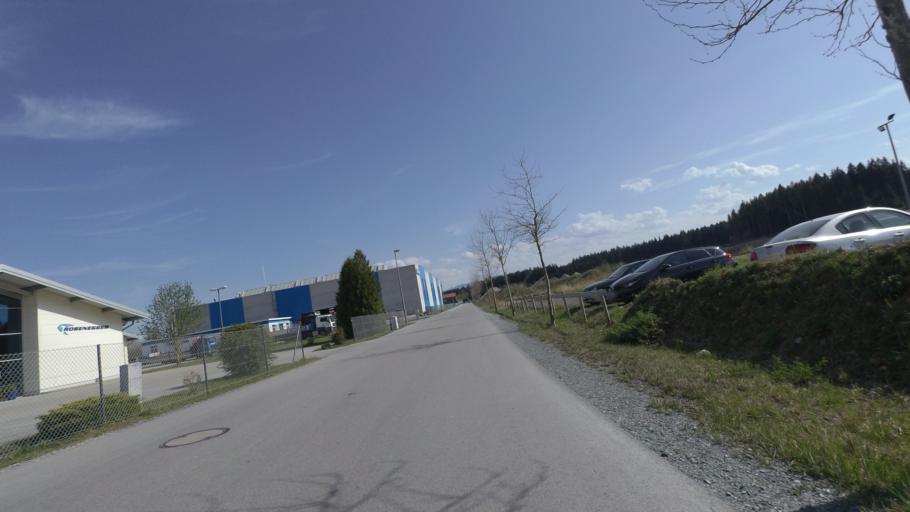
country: DE
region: Bavaria
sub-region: Upper Bavaria
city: Nussdorf
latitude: 47.9042
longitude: 12.6154
